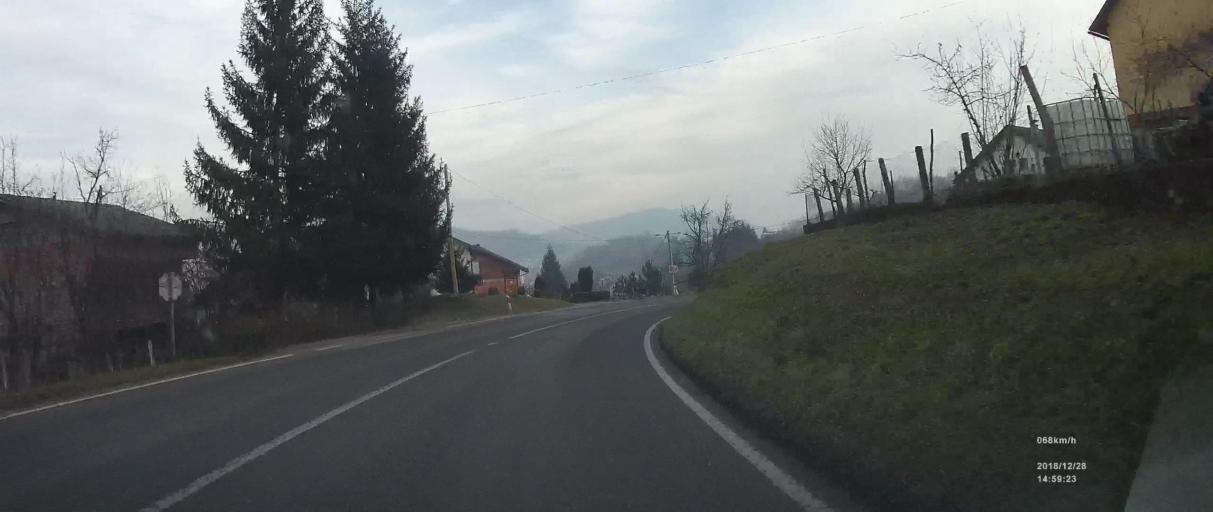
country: HR
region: Karlovacka
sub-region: Grad Karlovac
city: Karlovac
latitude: 45.4580
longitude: 15.4817
